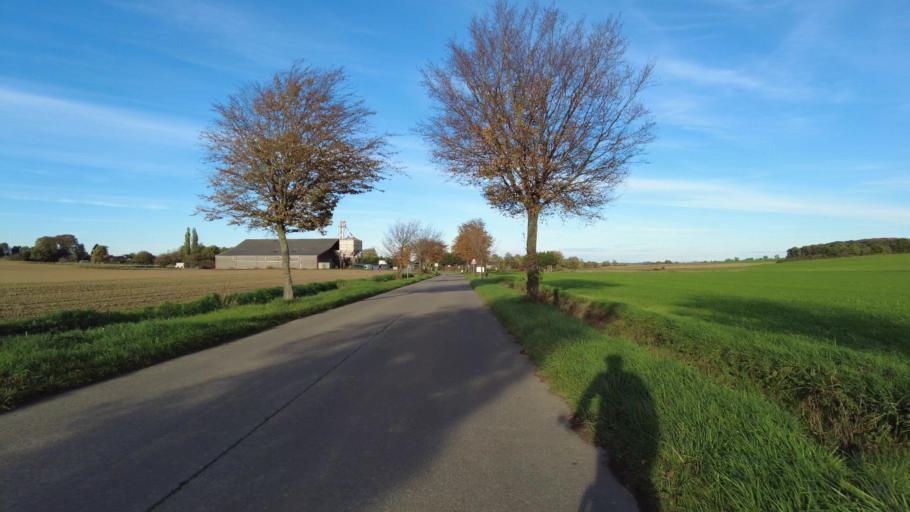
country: BE
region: Wallonia
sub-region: Province du Brabant Wallon
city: Jodoigne
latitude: 50.7095
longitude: 4.9186
